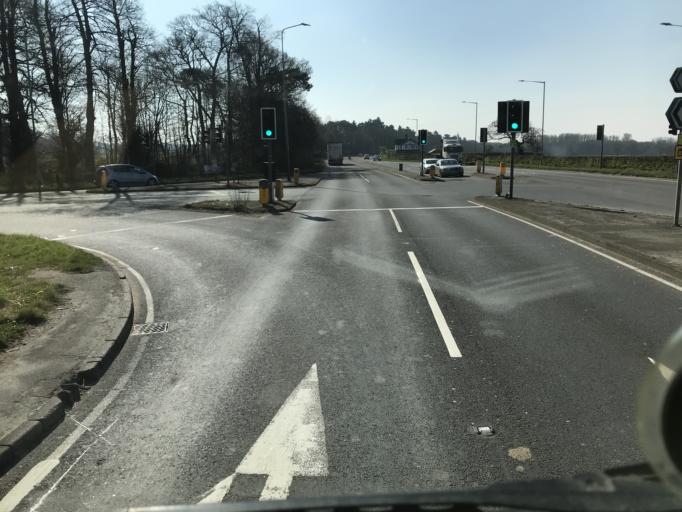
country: GB
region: England
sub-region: Cheshire East
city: Mere
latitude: 53.3018
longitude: -2.4192
